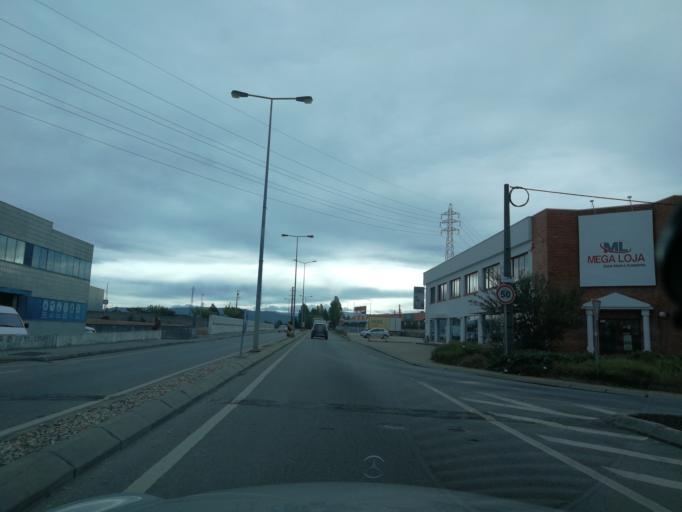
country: PT
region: Aveiro
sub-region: Agueda
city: Agueda
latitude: 40.5942
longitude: -8.4613
